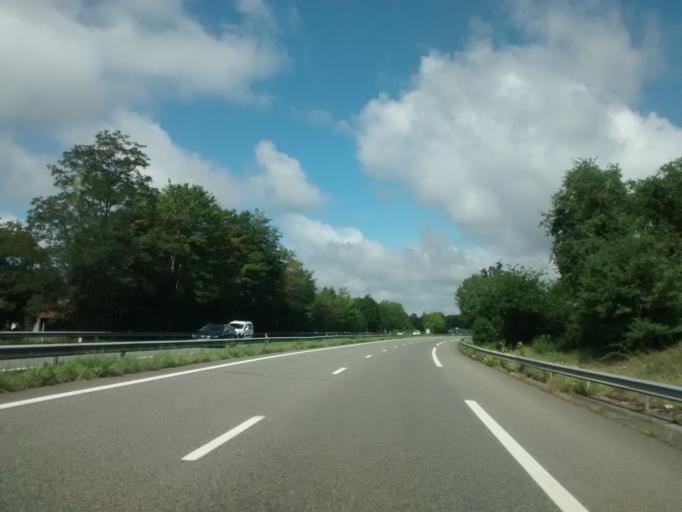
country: FR
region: Aquitaine
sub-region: Departement des Pyrenees-Atlantiques
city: Orthez
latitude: 43.4753
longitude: -0.7640
